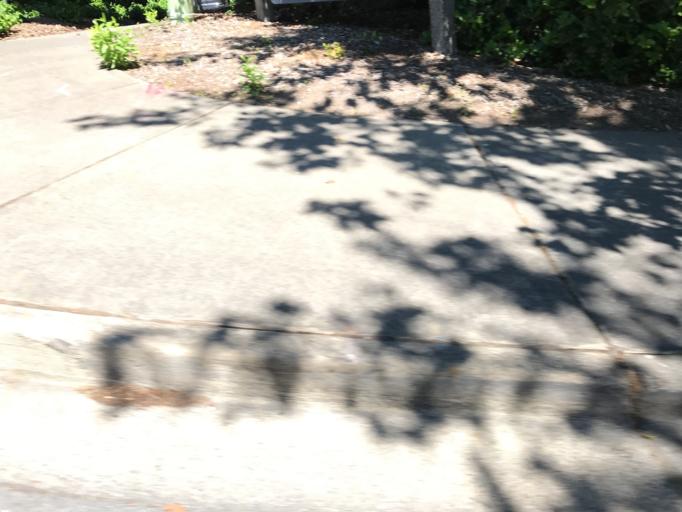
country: US
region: Washington
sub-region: King County
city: Redmond
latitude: 47.6460
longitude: -122.1239
